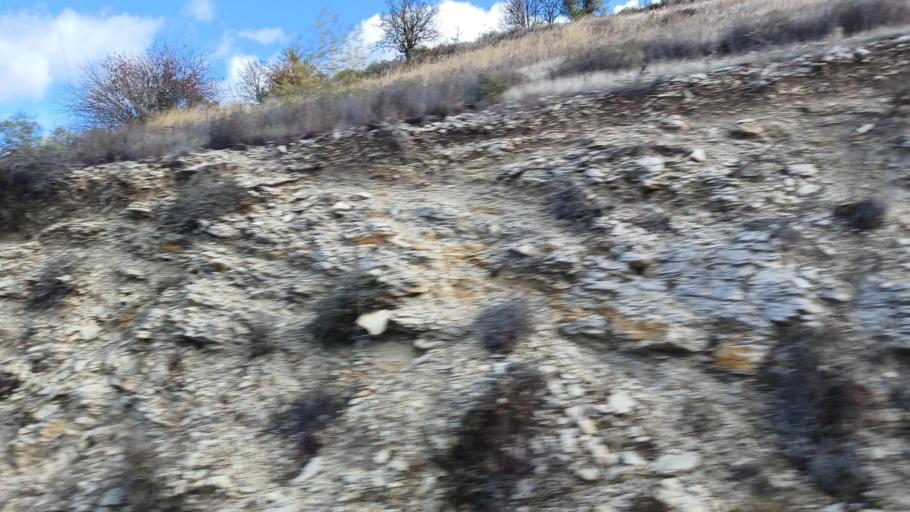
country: CY
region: Limassol
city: Pachna
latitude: 34.8572
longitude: 32.6943
